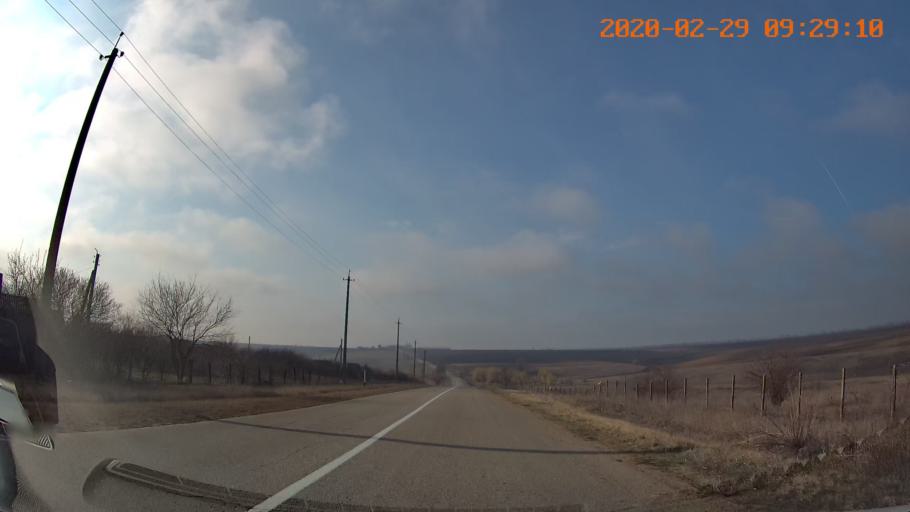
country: UA
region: Odessa
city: Lymanske
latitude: 46.6812
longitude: 29.9233
